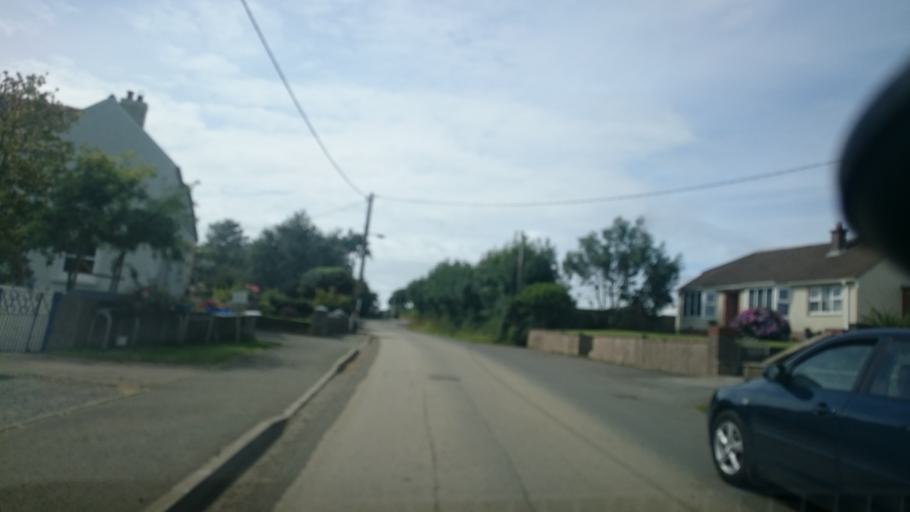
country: GB
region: Wales
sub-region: Pembrokeshire
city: Llangwm
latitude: 51.7498
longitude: -4.9164
